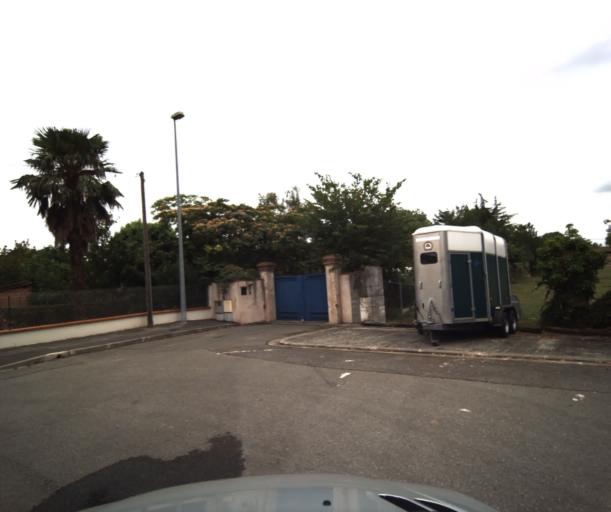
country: FR
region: Midi-Pyrenees
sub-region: Departement de la Haute-Garonne
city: Pinsaguel
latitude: 43.5030
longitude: 1.3936
